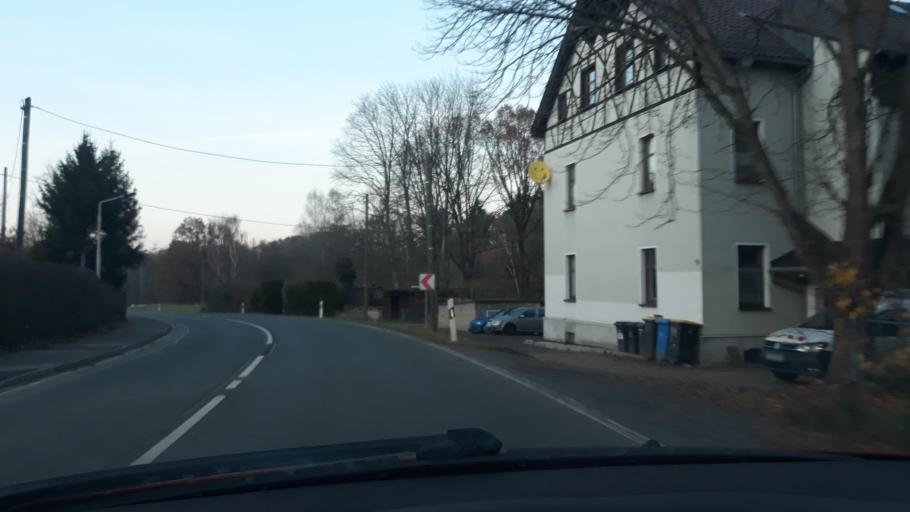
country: DE
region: Saxony
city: Wilkau-Hasslau
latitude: 50.6611
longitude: 12.5242
